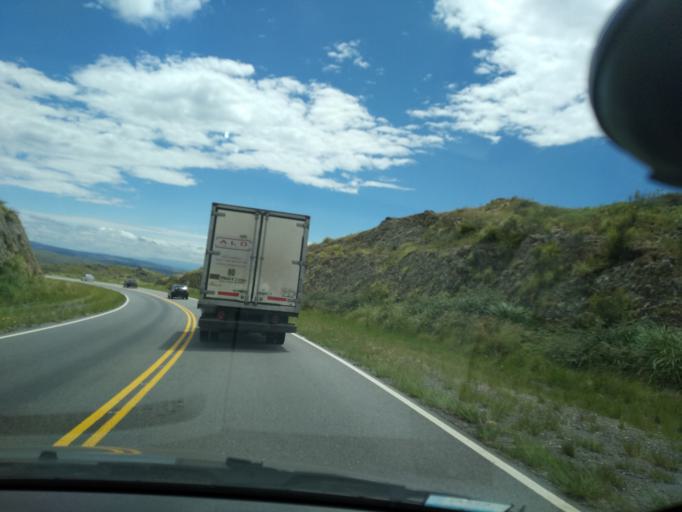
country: AR
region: Cordoba
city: Cuesta Blanca
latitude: -31.6210
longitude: -64.6684
